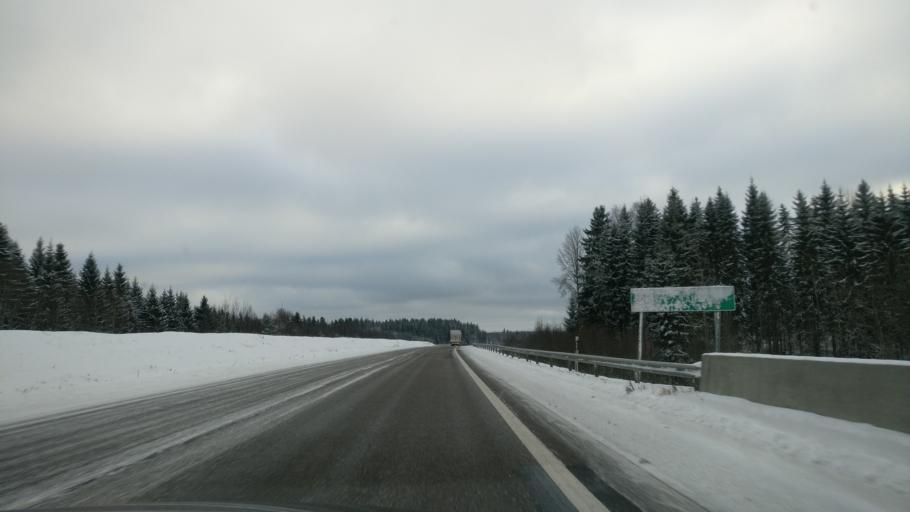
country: FI
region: Paijanne Tavastia
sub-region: Lahti
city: Nastola
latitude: 61.0854
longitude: 25.8940
